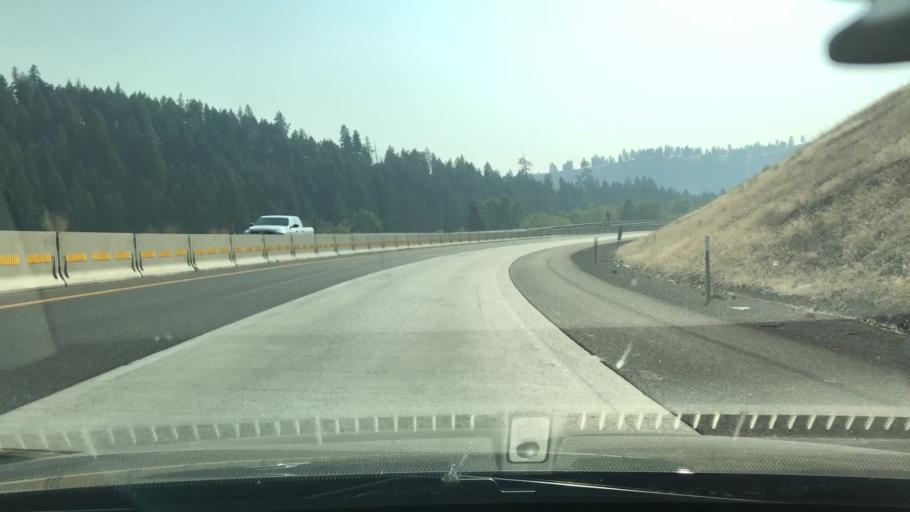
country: US
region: Oregon
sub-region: Union County
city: La Grande
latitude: 45.3427
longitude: -118.2278
